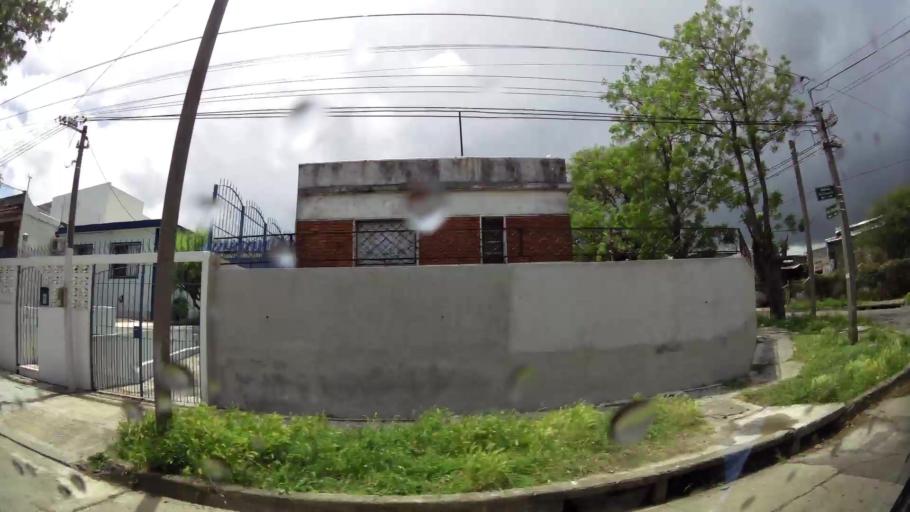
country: UY
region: Montevideo
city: Montevideo
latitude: -34.8565
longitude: -56.1660
